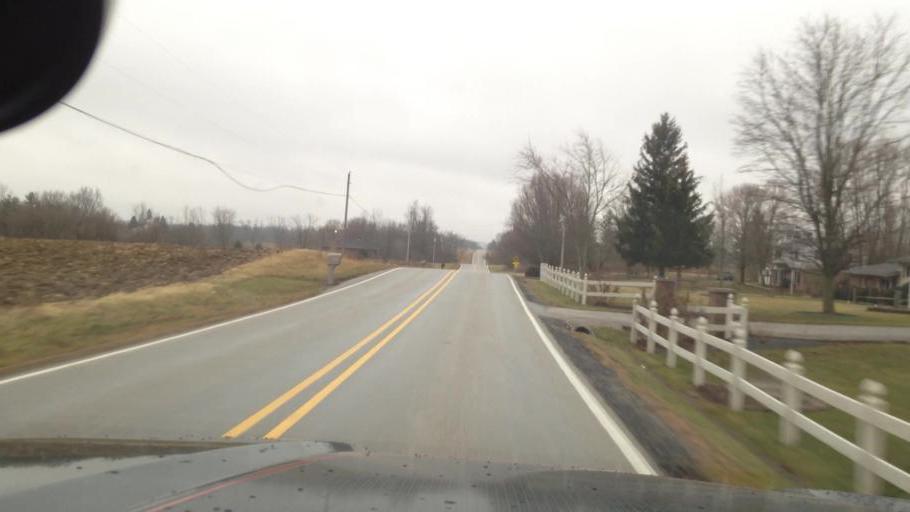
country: US
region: Ohio
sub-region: Preble County
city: New Paris
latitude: 39.9139
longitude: -84.8317
